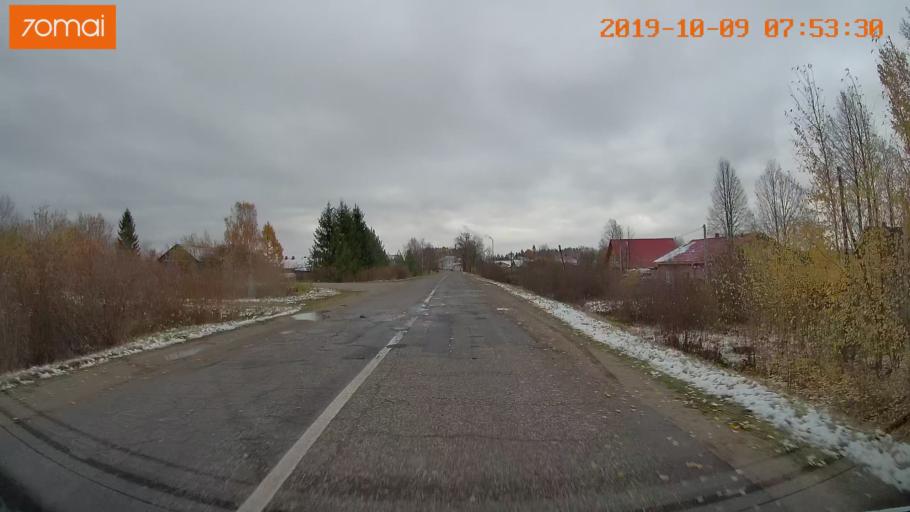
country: RU
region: Jaroslavl
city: Kukoboy
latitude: 58.6981
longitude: 39.8961
